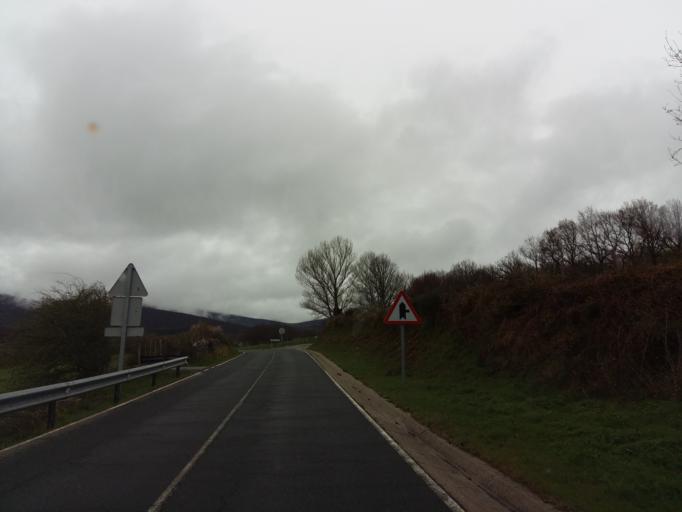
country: ES
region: Cantabria
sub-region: Provincia de Cantabria
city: Villaescusa
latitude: 42.9354
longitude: -4.2027
